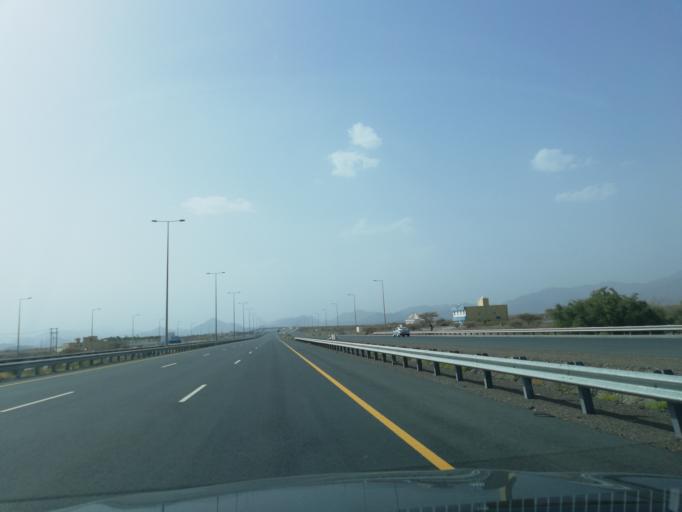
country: OM
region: Muhafazat ad Dakhiliyah
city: Sufalat Sama'il
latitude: 23.0318
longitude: 58.2052
